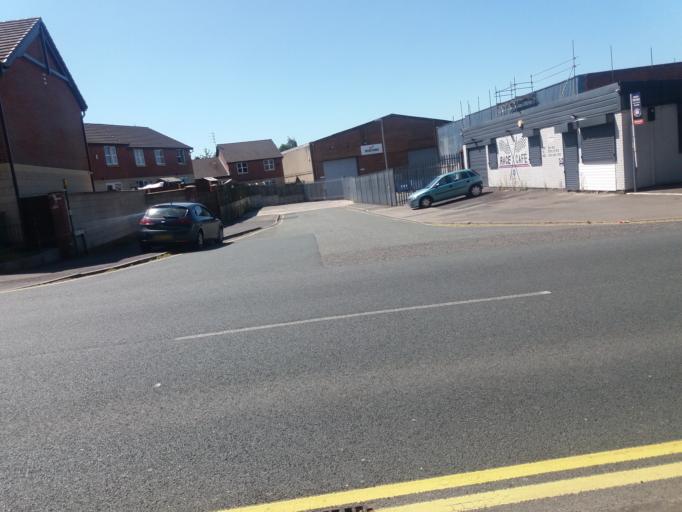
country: GB
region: England
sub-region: Lancashire
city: Preston
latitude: 53.7582
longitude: -2.7115
